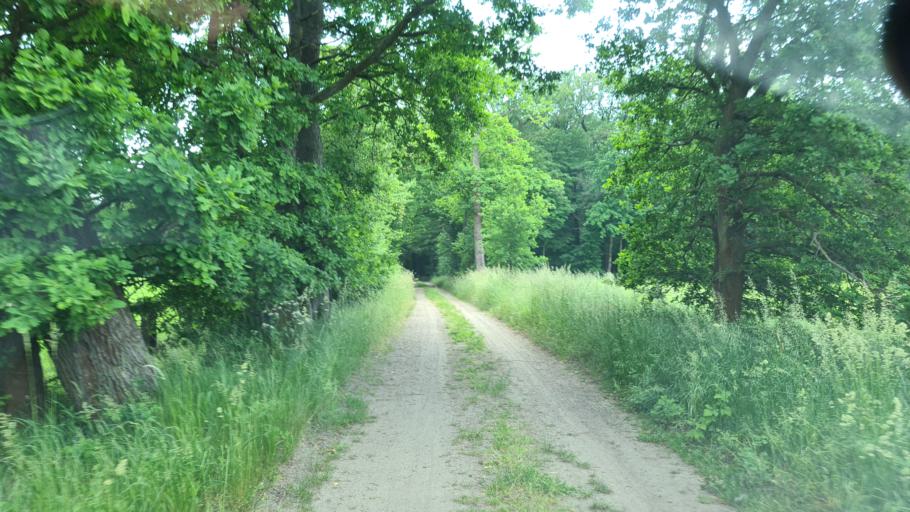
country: DE
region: Brandenburg
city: Sonnewalde
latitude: 51.7046
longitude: 13.6367
